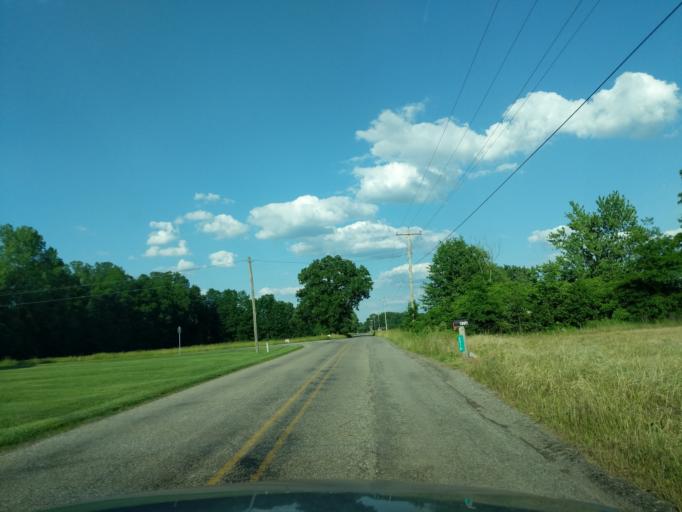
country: US
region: Indiana
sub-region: Whitley County
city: Tri-Lakes
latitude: 41.3023
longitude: -85.5107
